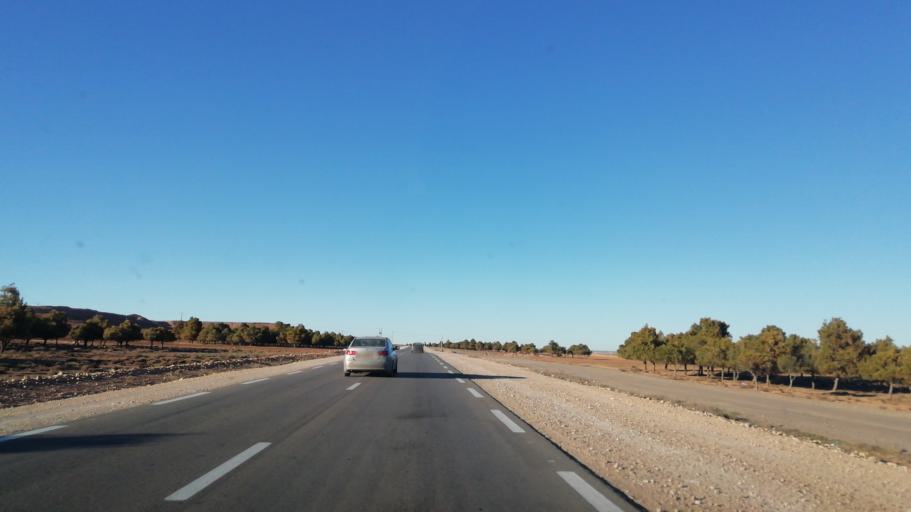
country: DZ
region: Tlemcen
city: Sebdou
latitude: 34.4967
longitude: -1.2760
